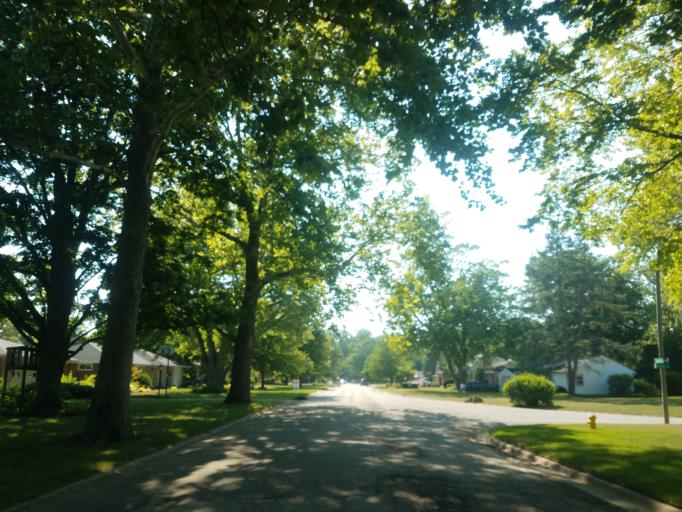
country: US
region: Illinois
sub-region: McLean County
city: Bloomington
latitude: 40.4754
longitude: -88.9604
